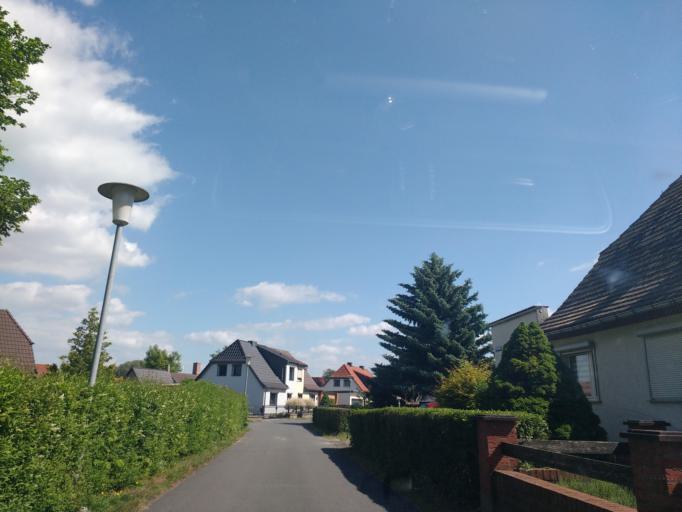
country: DE
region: Saxony-Anhalt
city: Roblingen am See
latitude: 51.4556
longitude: 11.6689
